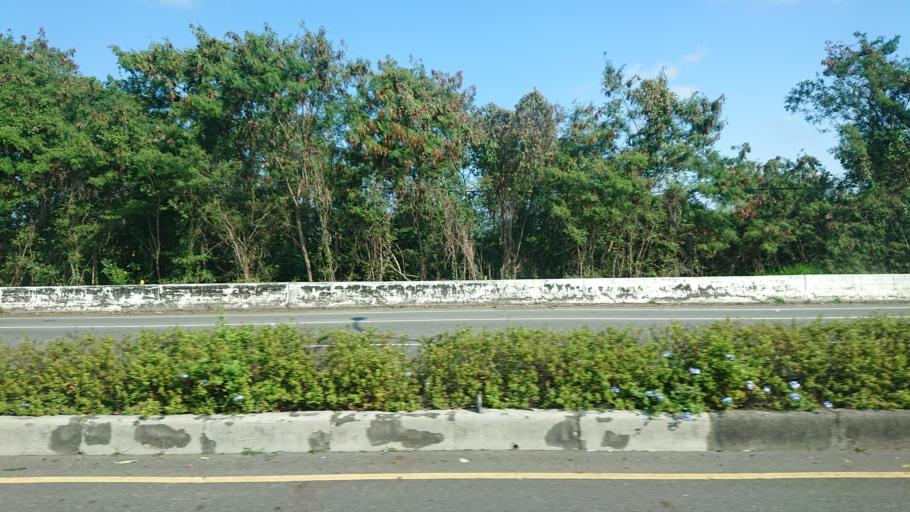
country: TW
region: Taiwan
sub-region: Chiayi
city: Taibao
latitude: 23.4428
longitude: 120.3741
